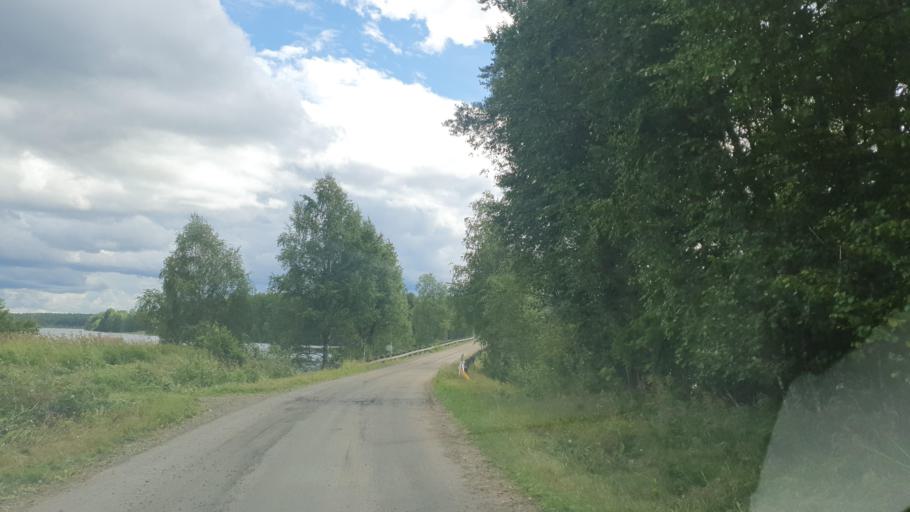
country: FI
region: Kainuu
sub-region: Kehys-Kainuu
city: Kuhmo
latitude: 64.0879
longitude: 29.0953
